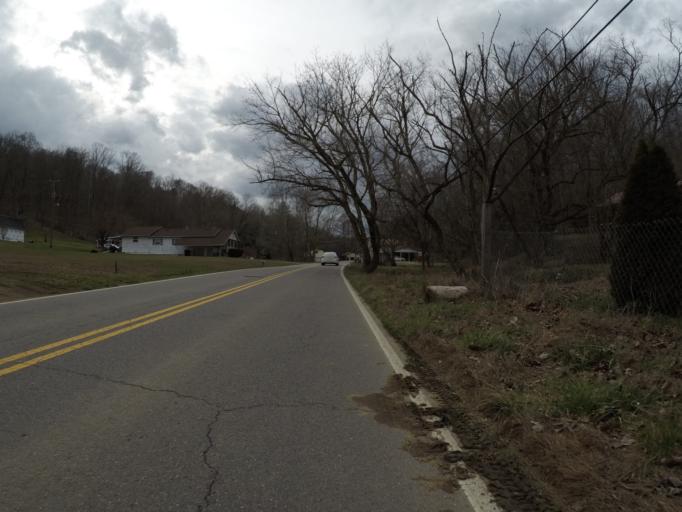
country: US
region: Ohio
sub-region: Lawrence County
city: Burlington
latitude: 38.4265
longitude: -82.5136
